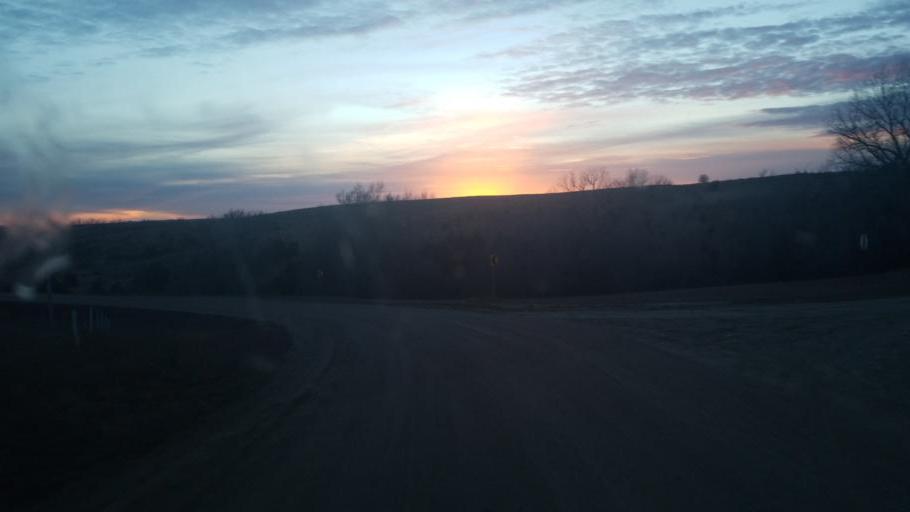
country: US
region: Nebraska
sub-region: Knox County
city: Center
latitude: 42.6258
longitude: -97.8371
